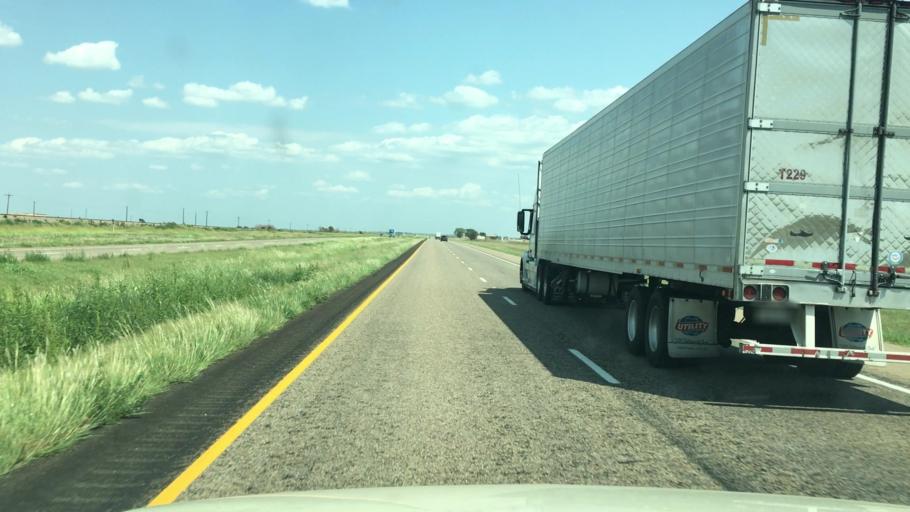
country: US
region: Texas
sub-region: Armstrong County
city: Claude
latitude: 35.0319
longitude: -101.1294
